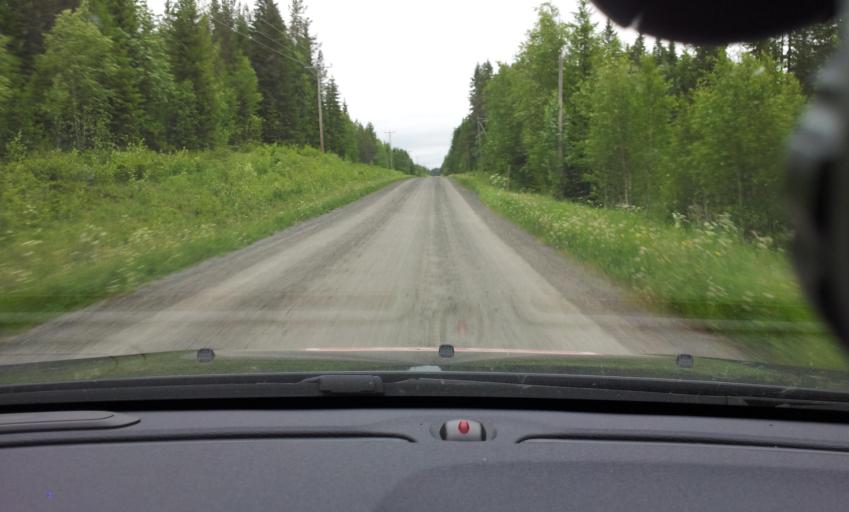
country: SE
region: Jaemtland
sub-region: Krokoms Kommun
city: Valla
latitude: 63.2462
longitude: 13.9659
